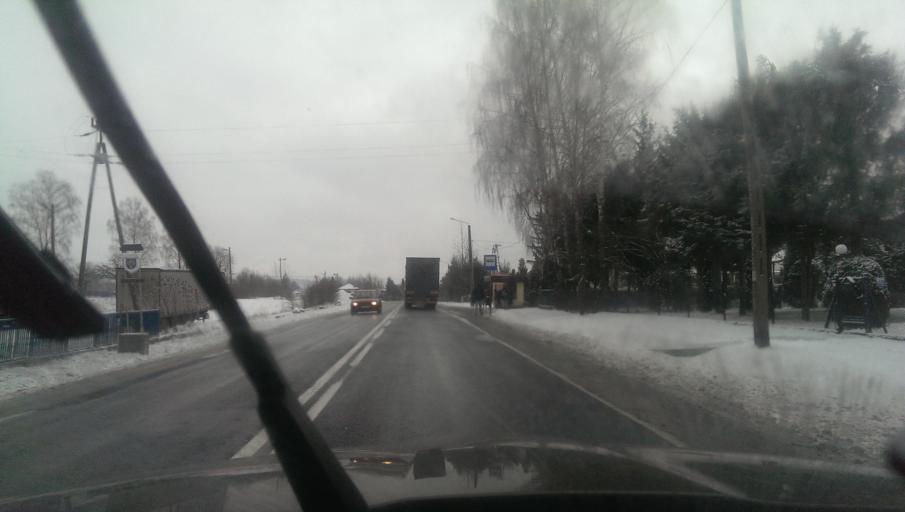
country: PL
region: Subcarpathian Voivodeship
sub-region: Powiat sanocki
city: Nowosielce-Gniewosz
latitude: 49.5620
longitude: 22.0854
